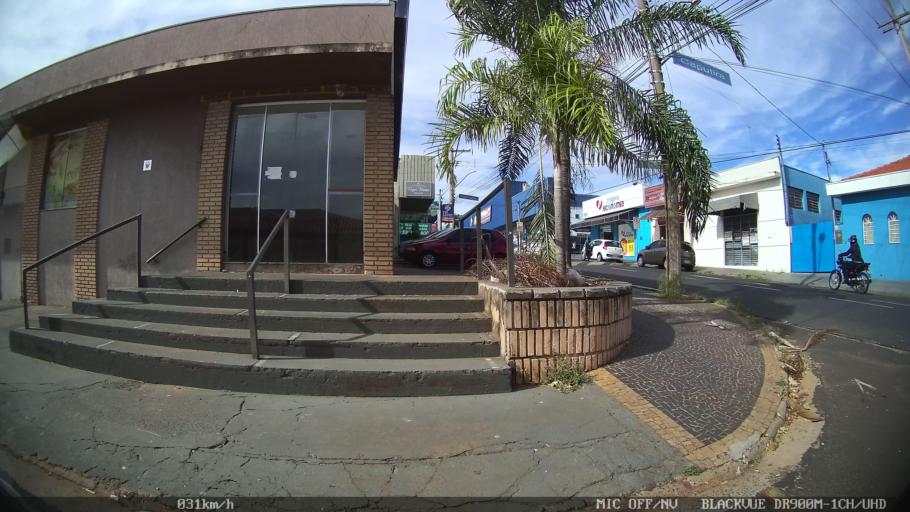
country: BR
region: Sao Paulo
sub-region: Catanduva
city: Catanduva
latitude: -21.1437
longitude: -48.9667
